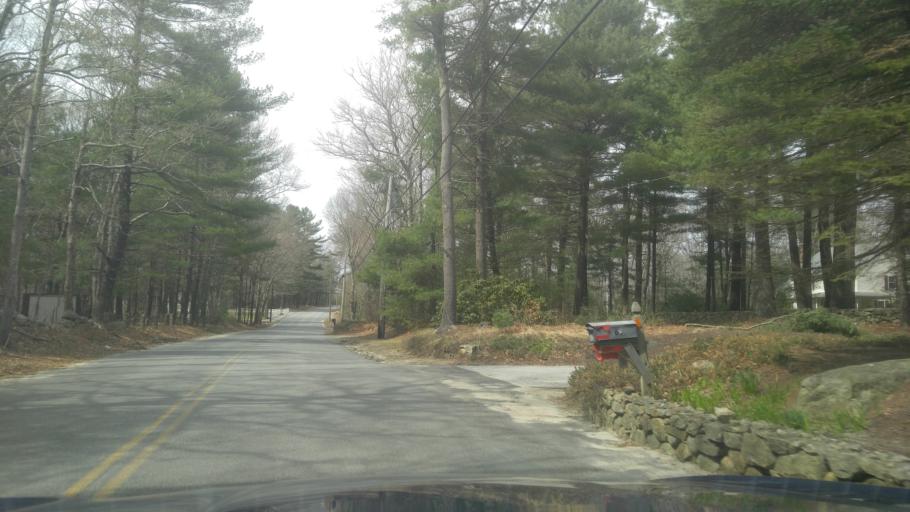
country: US
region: Rhode Island
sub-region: Washington County
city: Exeter
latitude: 41.6235
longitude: -71.5652
